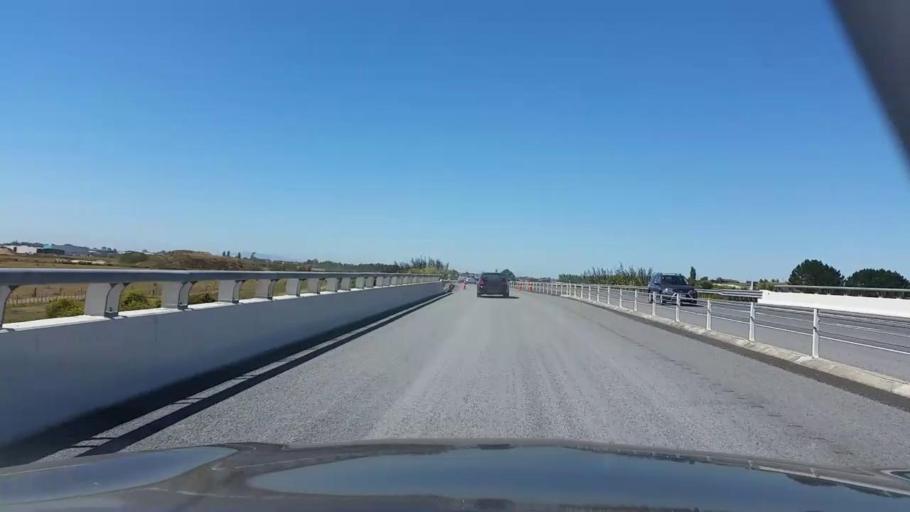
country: NZ
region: Waikato
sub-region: Hamilton City
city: Hamilton
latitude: -37.7478
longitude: 175.2159
